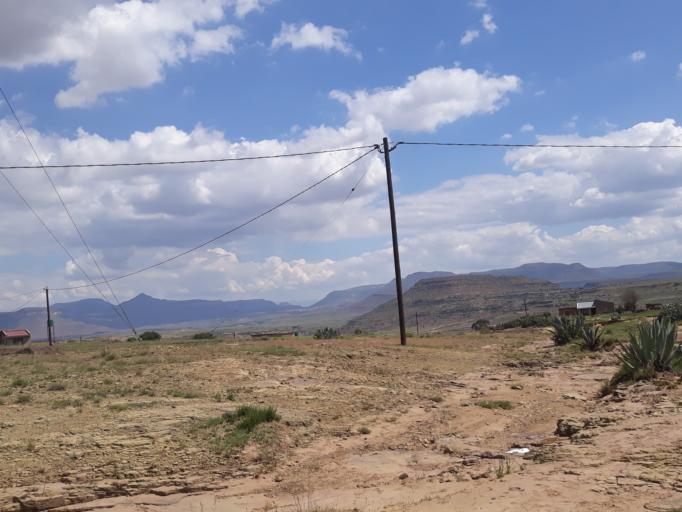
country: LS
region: Quthing
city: Quthing
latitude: -30.3414
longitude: 27.5301
